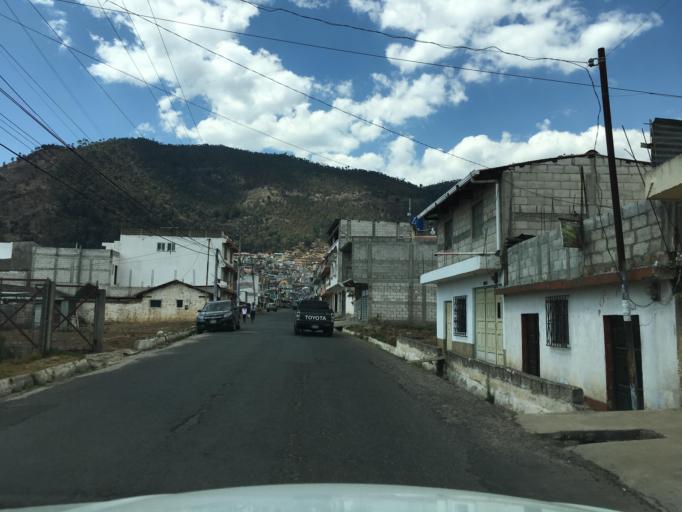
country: GT
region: Totonicapan
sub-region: Municipio de San Andres Xecul
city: San Andres Xecul
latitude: 14.9051
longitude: -91.4773
